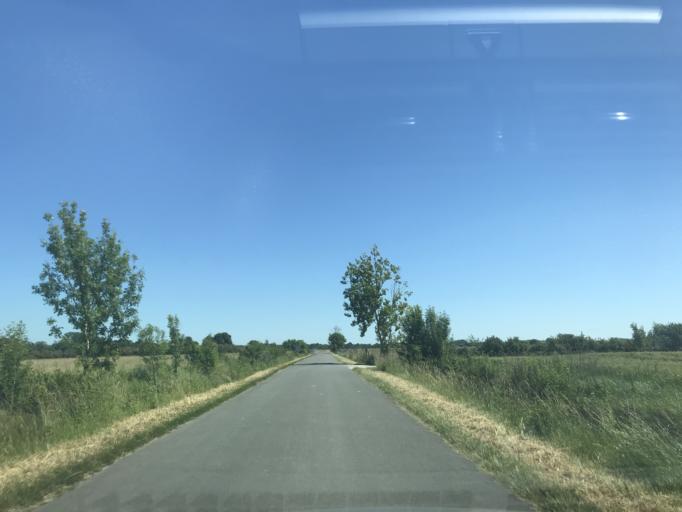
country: FR
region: Poitou-Charentes
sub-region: Departement de la Charente-Maritime
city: Mortagne-sur-Gironde
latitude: 45.4485
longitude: -0.7614
